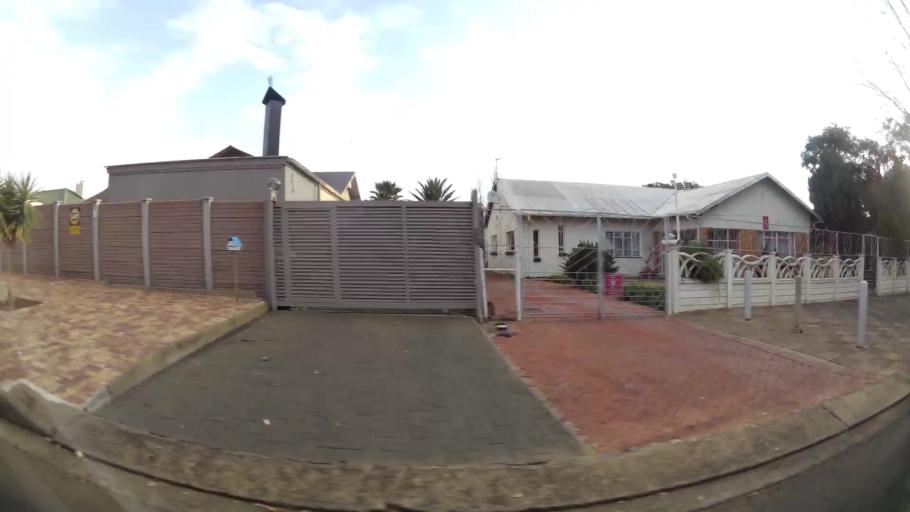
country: ZA
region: Orange Free State
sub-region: Mangaung Metropolitan Municipality
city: Bloemfontein
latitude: -29.1391
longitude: 26.1968
